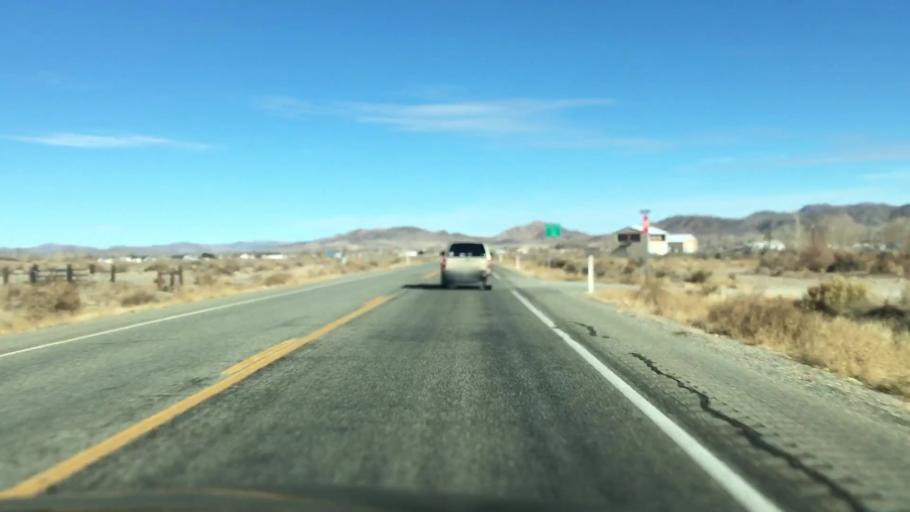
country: US
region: Nevada
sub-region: Lyon County
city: Yerington
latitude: 39.0047
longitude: -119.0888
